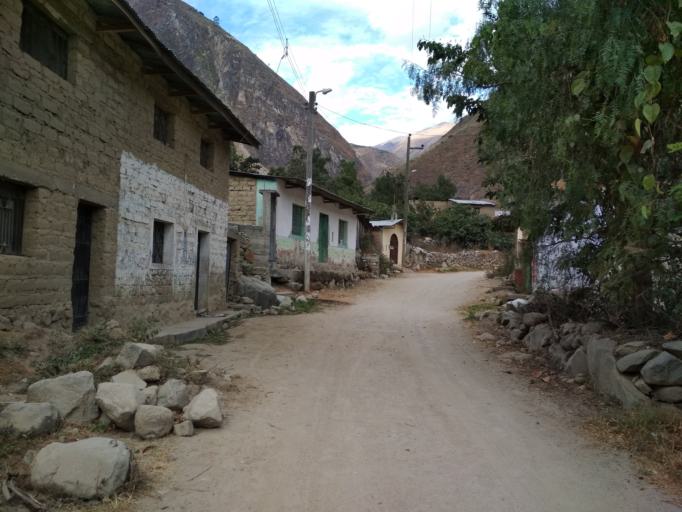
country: PE
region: Lima
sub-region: Provincia de Yauyos
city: Cacra
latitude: -12.8226
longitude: -75.7949
